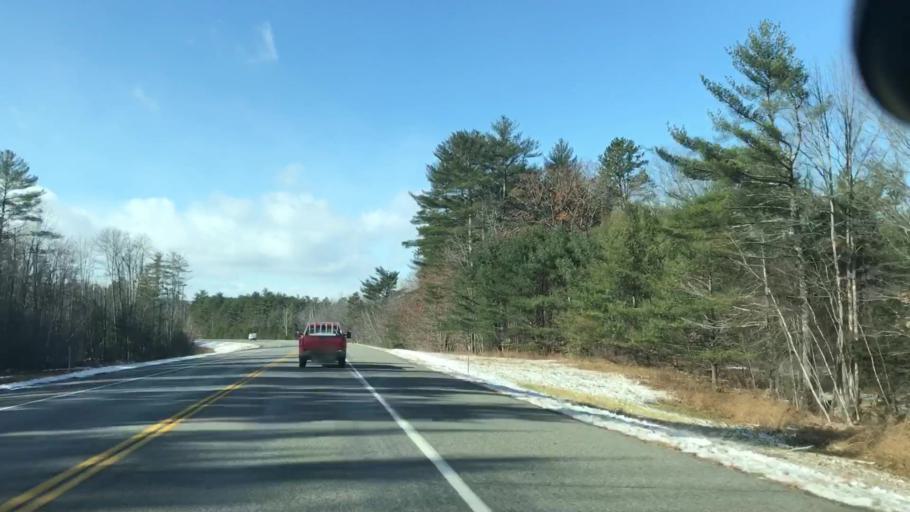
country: US
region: New Hampshire
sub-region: Carroll County
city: Freedom
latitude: 43.7928
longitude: -71.0666
